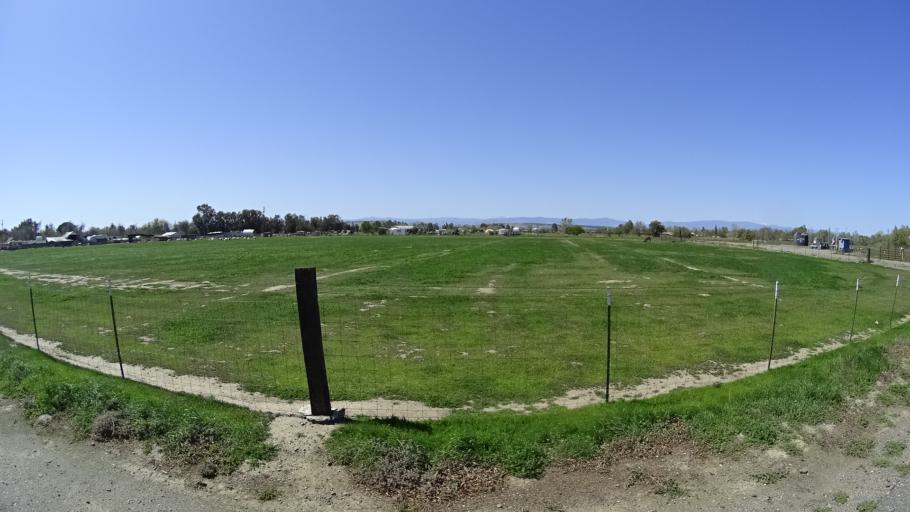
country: US
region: California
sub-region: Glenn County
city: Orland
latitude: 39.7824
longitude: -122.2386
